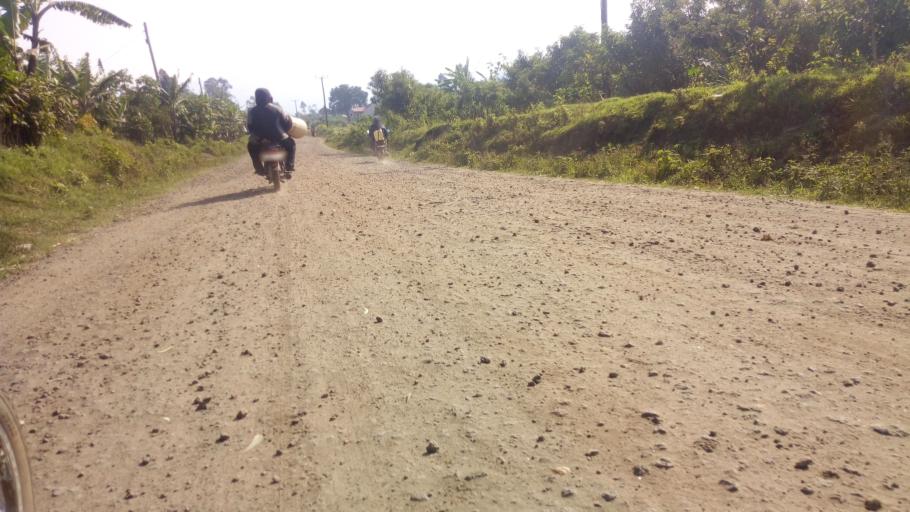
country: UG
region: Western Region
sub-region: Kisoro District
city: Kisoro
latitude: -1.2546
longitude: 29.7135
